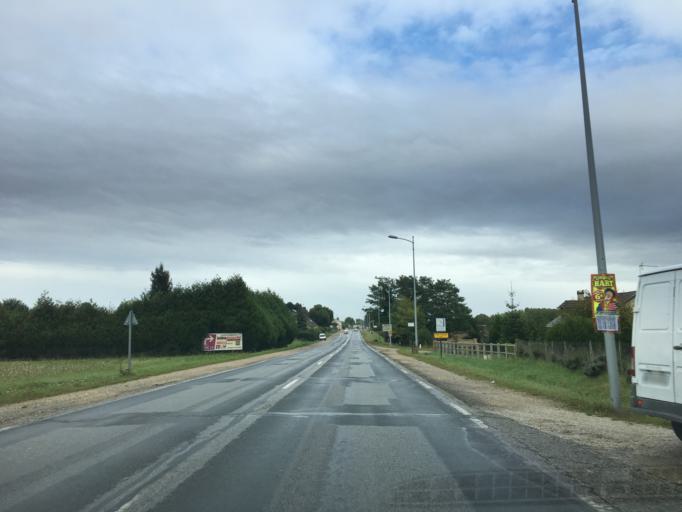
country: FR
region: Haute-Normandie
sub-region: Departement de l'Eure
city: Verneuil-sur-Avre
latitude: 48.7389
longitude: 0.9085
